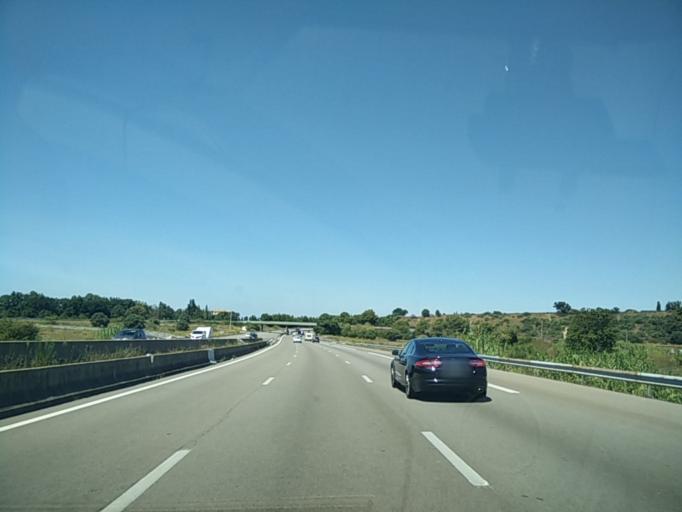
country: FR
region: Provence-Alpes-Cote d'Azur
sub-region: Departement des Bouches-du-Rhone
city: Noves
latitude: 43.8949
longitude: 4.9189
